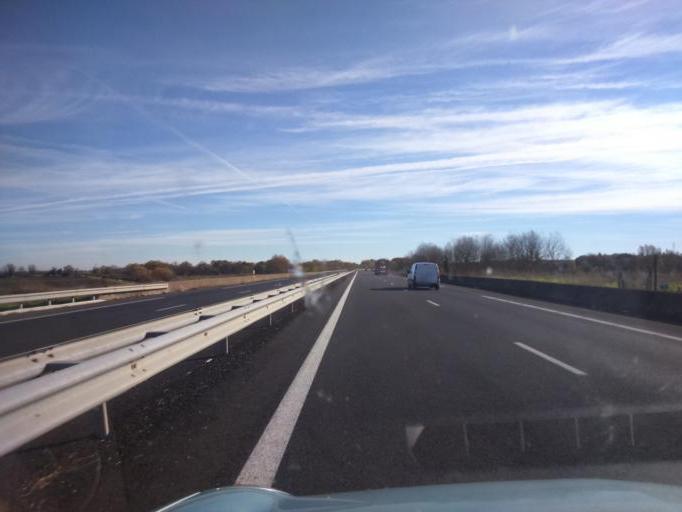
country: FR
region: Poitou-Charentes
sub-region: Departement de la Charente-Maritime
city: Tonnay-Charente
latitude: 45.9575
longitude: -0.9239
